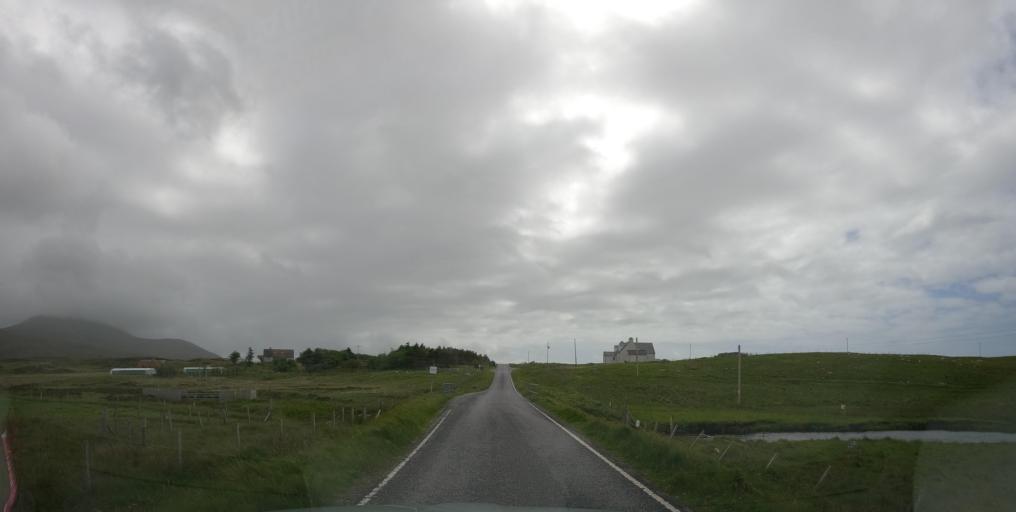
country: GB
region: Scotland
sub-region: Eilean Siar
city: Isle of South Uist
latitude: 57.2883
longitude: -7.3665
